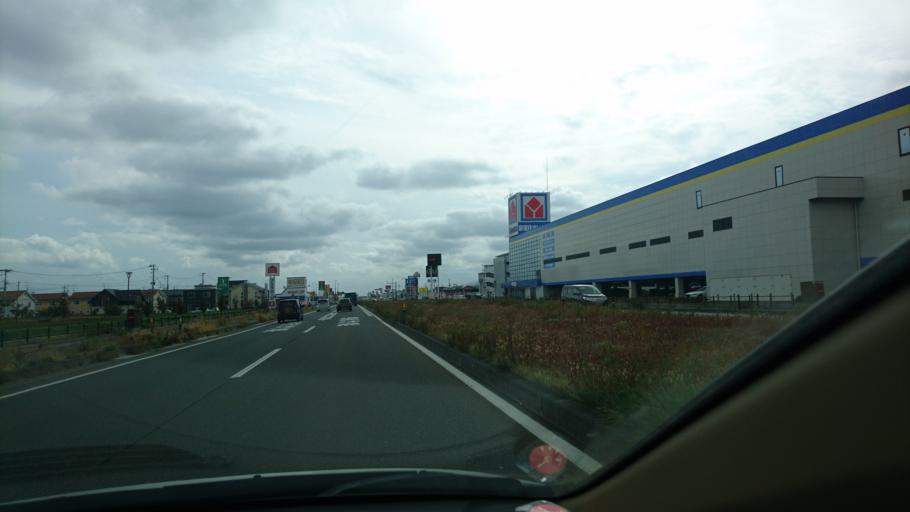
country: JP
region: Iwate
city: Morioka-shi
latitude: 39.6797
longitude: 141.1354
